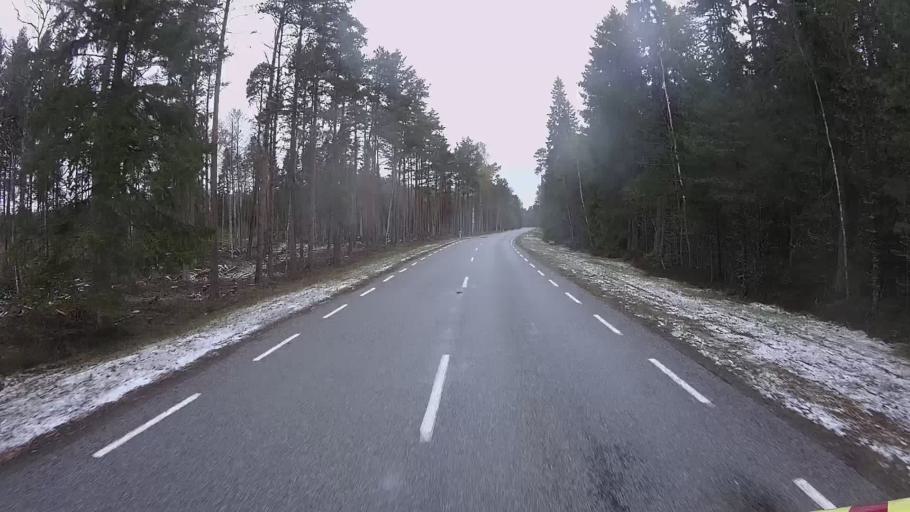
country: EE
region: Hiiumaa
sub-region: Kaerdla linn
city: Kardla
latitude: 59.0465
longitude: 22.6814
